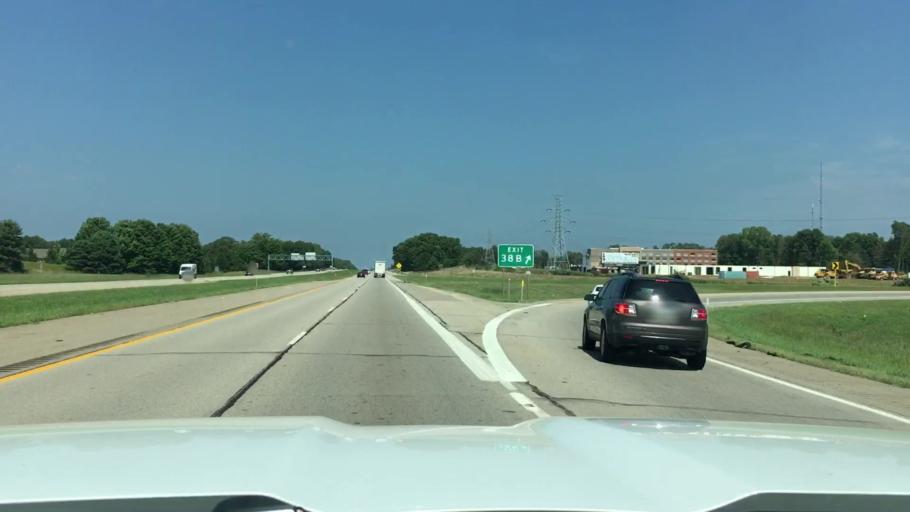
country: US
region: Michigan
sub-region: Kalamazoo County
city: Westwood
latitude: 42.2964
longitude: -85.6636
